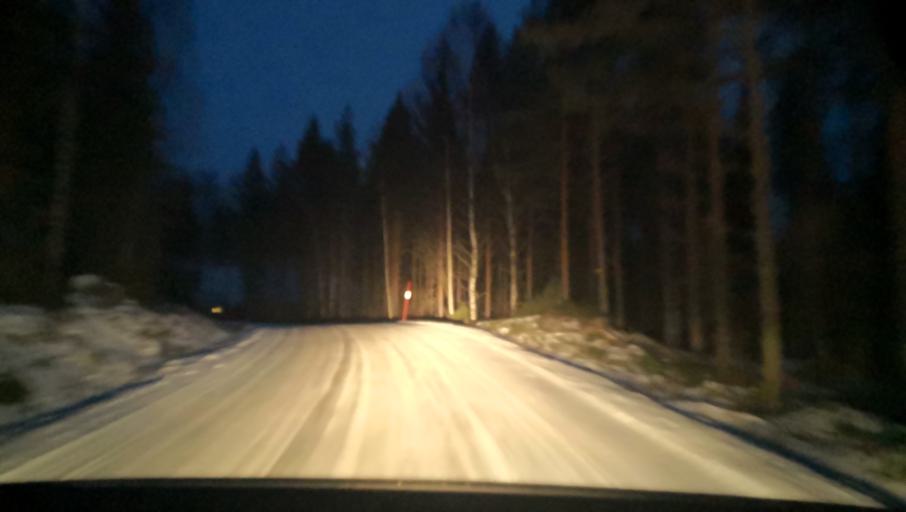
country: SE
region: Uppsala
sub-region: Heby Kommun
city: Tarnsjo
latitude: 60.2518
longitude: 16.7559
